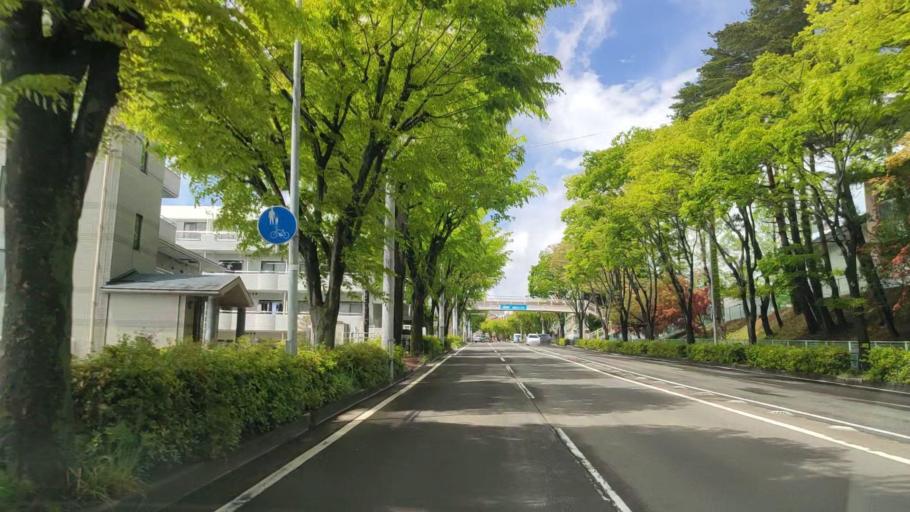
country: JP
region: Miyagi
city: Sendai
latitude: 38.2387
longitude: 140.8482
